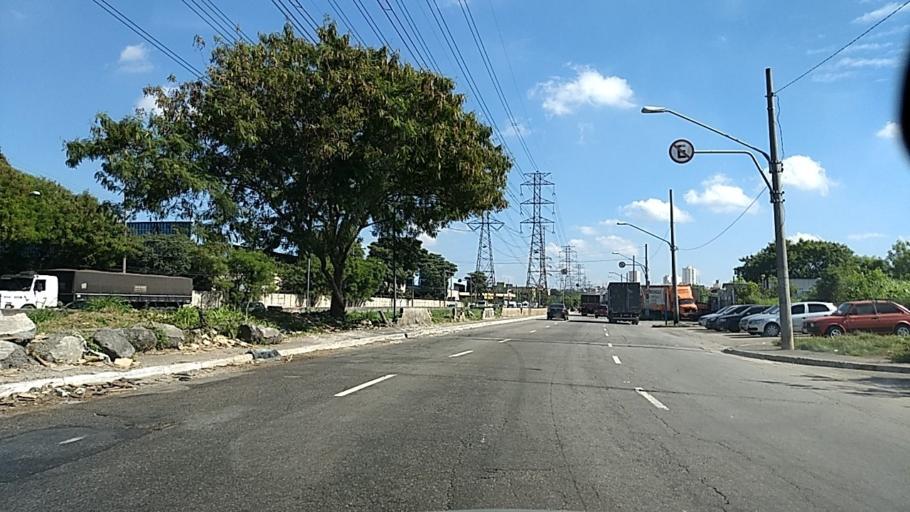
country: BR
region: Sao Paulo
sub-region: Guarulhos
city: Guarulhos
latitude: -23.4889
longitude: -46.5620
